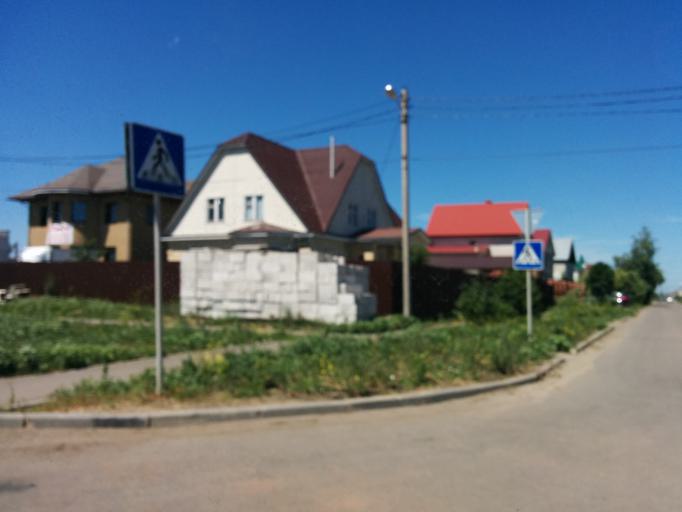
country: RU
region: Tambov
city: Tambov
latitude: 52.7787
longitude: 41.3814
